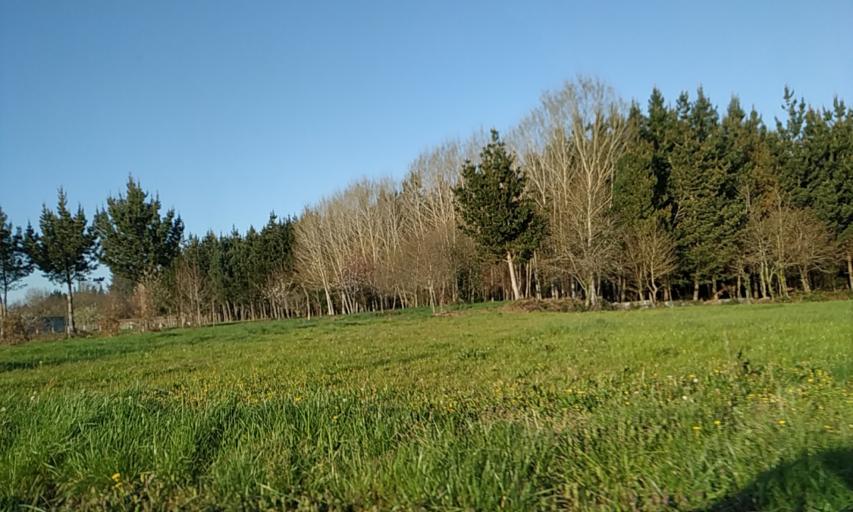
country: ES
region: Galicia
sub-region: Provincia de Lugo
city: Corgo
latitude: 42.9354
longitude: -7.3985
